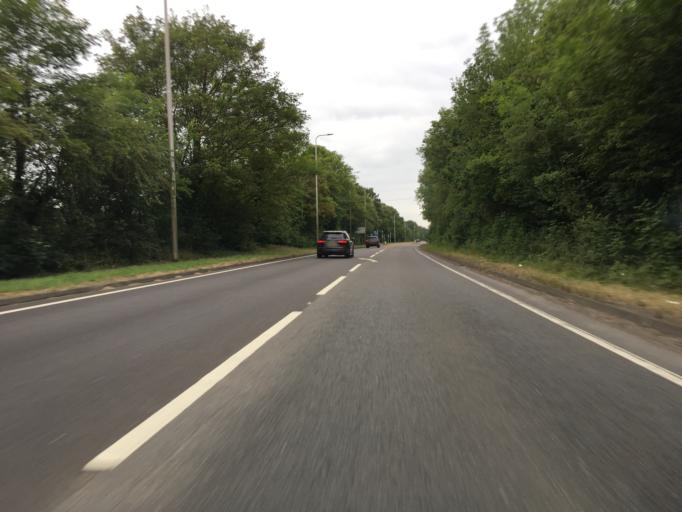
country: GB
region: England
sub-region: Hertfordshire
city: Flamstead
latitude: 51.8305
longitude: -0.4488
